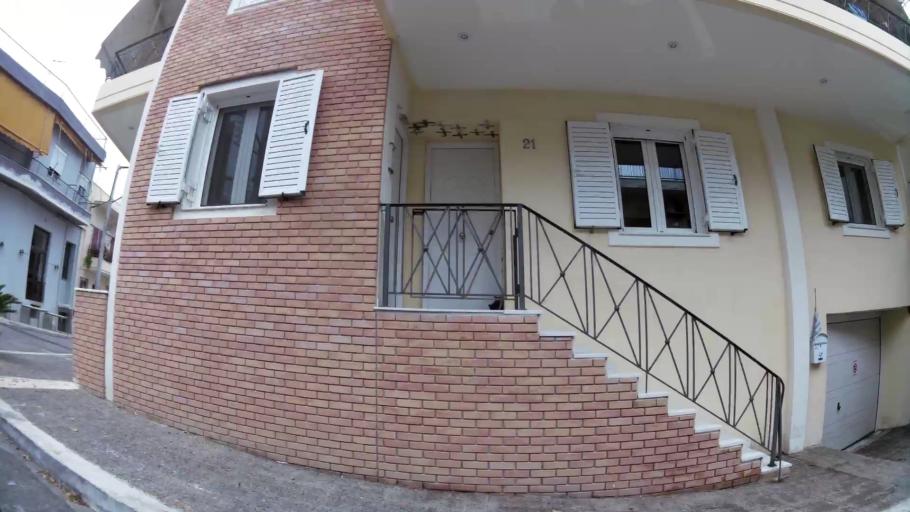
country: GR
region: Attica
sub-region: Nomos Attikis
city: Piraeus
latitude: 37.9411
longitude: 23.6568
